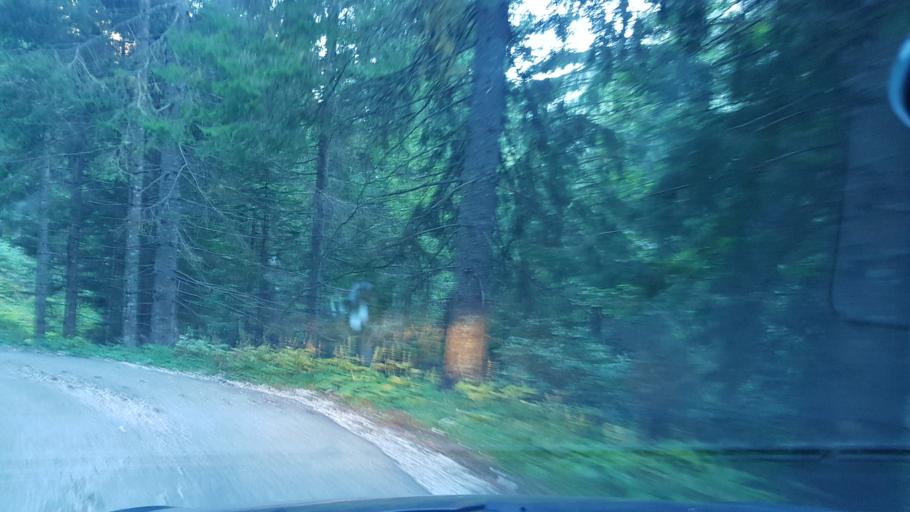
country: IT
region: Veneto
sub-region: Provincia di Belluno
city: Fusine
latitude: 46.3497
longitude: 12.0927
